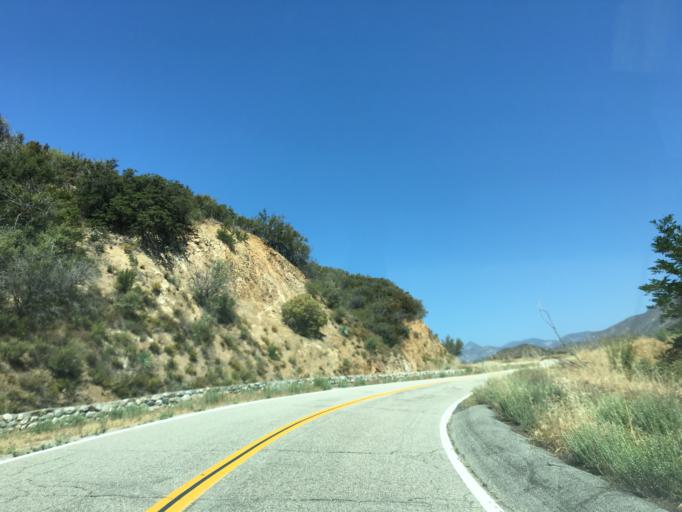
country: US
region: California
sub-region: Los Angeles County
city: San Dimas
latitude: 34.2269
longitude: -117.7775
